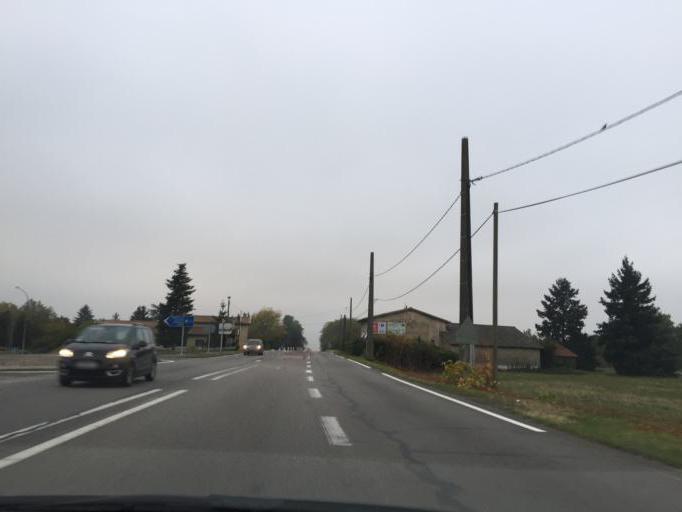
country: FR
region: Rhone-Alpes
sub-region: Departement de l'Isere
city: Roussillon
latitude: 45.3912
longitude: 4.8051
